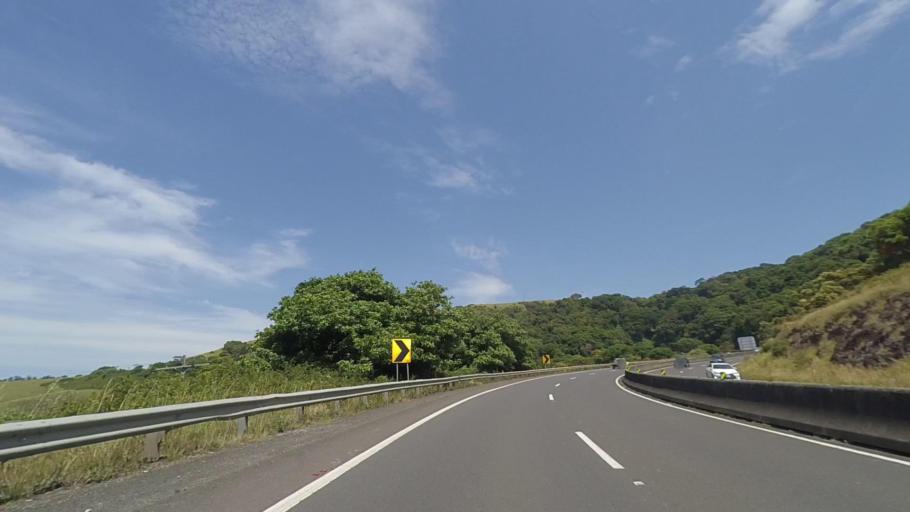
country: AU
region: New South Wales
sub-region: Kiama
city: Kiama
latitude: -34.7005
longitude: 150.8393
